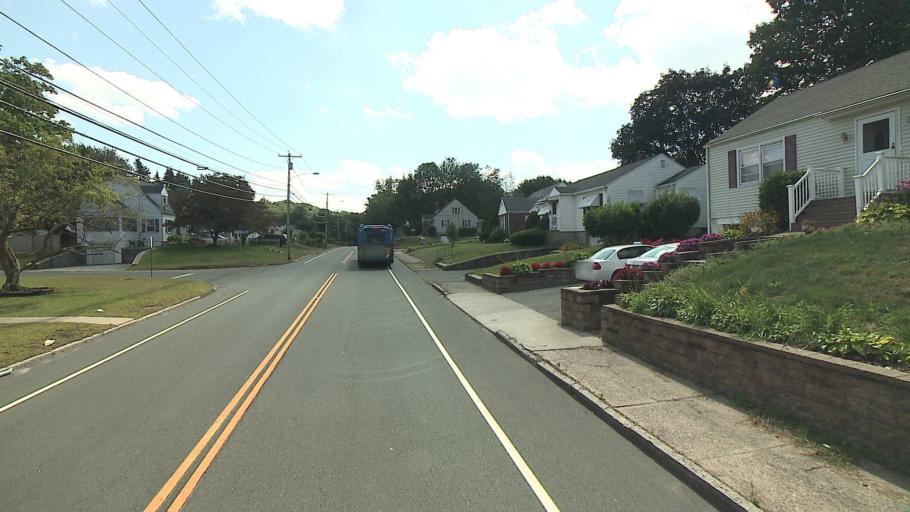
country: US
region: Connecticut
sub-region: New Haven County
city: Ansonia
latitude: 41.3601
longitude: -73.0823
